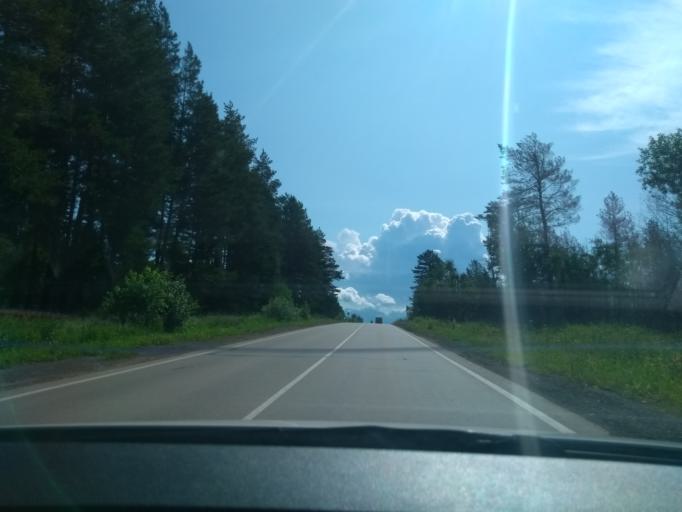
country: RU
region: Perm
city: Bershet'
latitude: 57.8256
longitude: 56.4190
